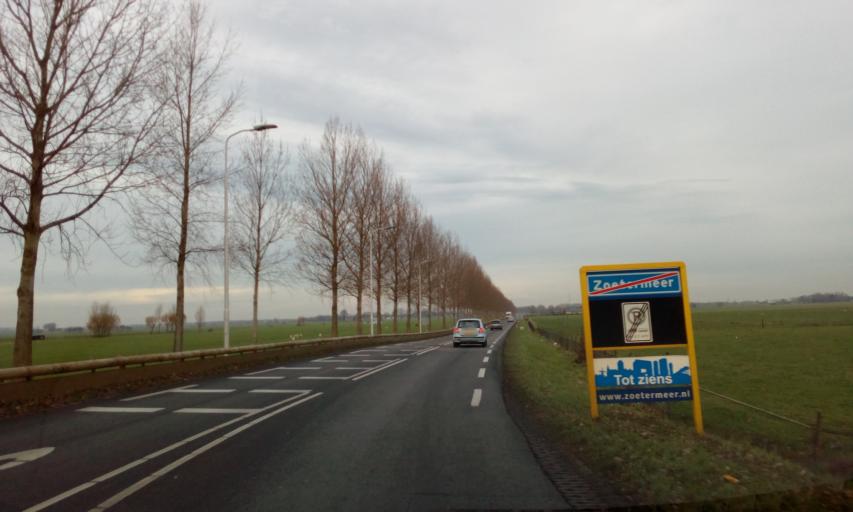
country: NL
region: South Holland
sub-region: Gemeente Zoetermeer
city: Zoetermeer
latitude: 52.0722
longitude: 4.4792
